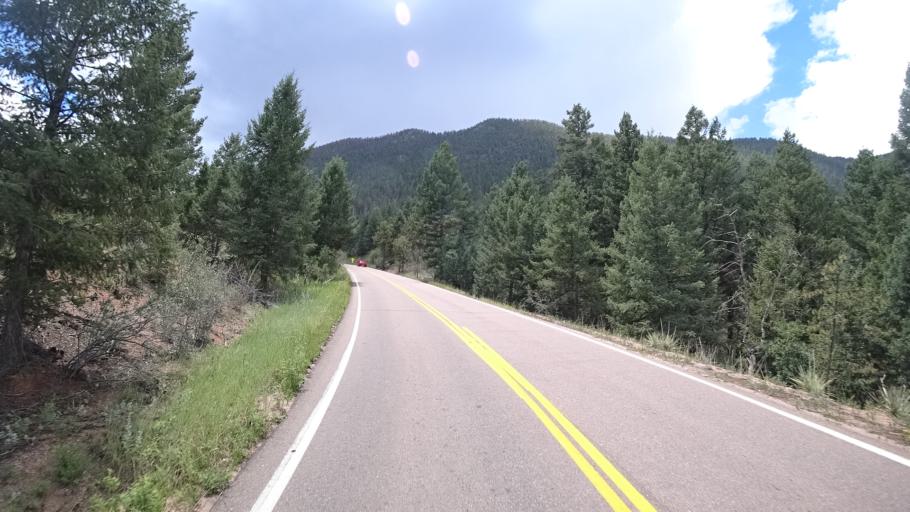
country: US
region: Colorado
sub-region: El Paso County
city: Cascade-Chipita Park
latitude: 38.9097
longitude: -104.9835
